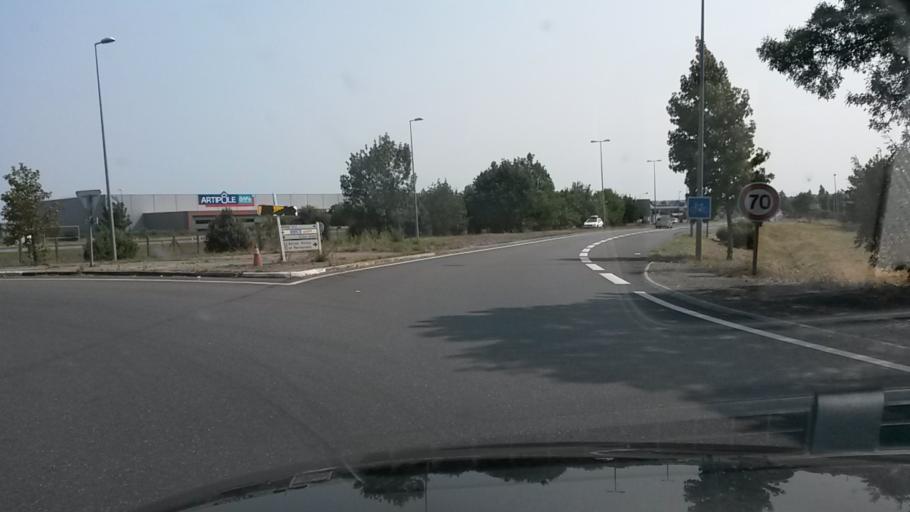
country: FR
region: Pays de la Loire
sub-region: Departement de la Loire-Atlantique
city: Saint-Gereon
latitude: 47.3993
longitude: -1.1906
